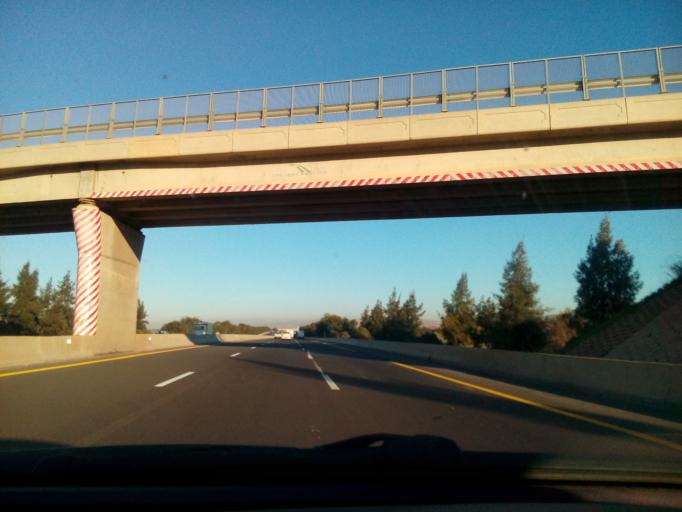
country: DZ
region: Relizane
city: Djidiouia
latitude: 35.9141
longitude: 0.7463
